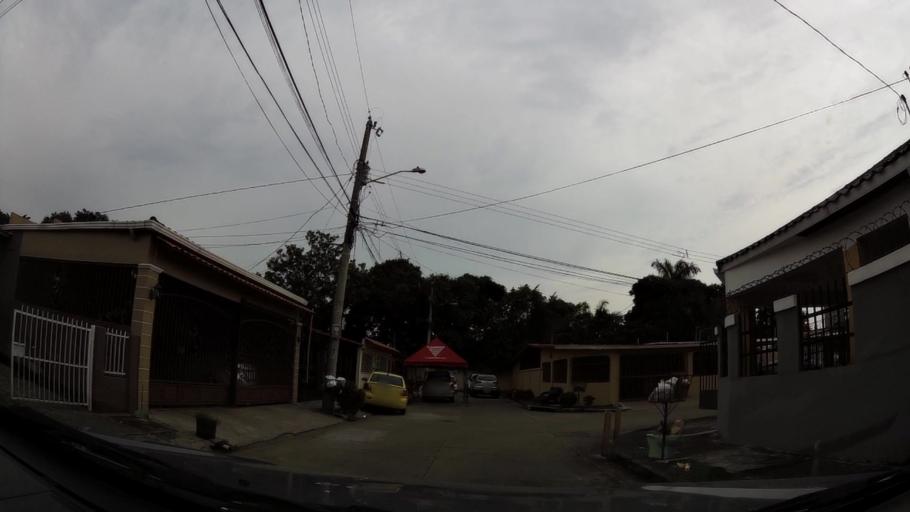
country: PA
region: Panama
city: San Miguelito
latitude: 9.0303
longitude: -79.4692
